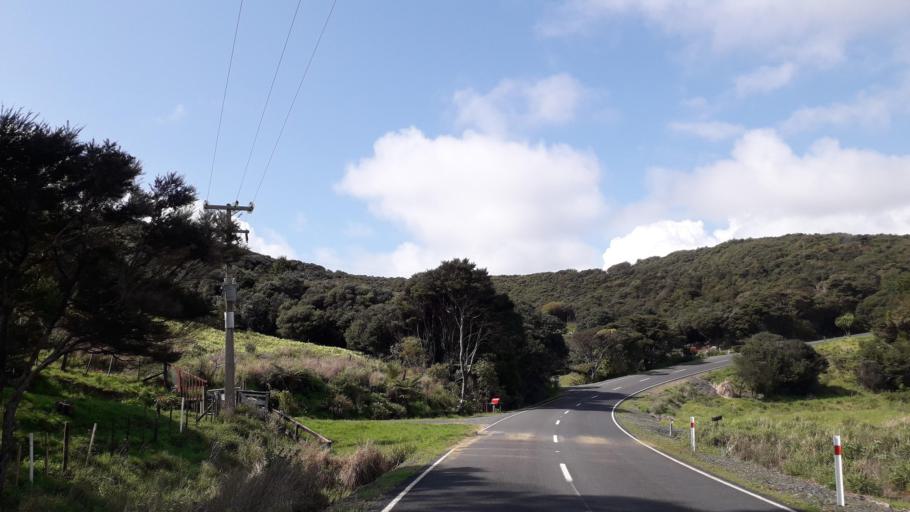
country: NZ
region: Northland
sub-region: Far North District
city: Paihia
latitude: -35.2450
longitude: 174.2551
